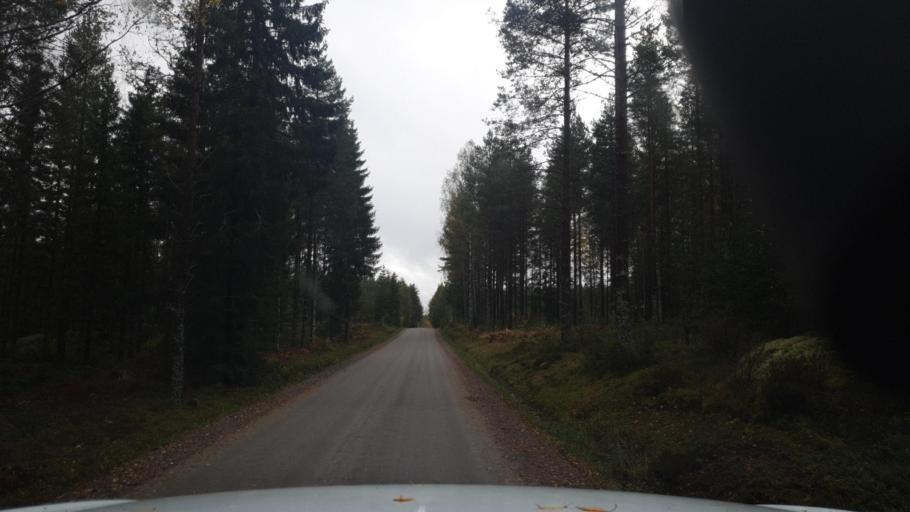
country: SE
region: Vaermland
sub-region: Karlstads Kommun
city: Edsvalla
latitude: 59.5279
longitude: 13.0005
